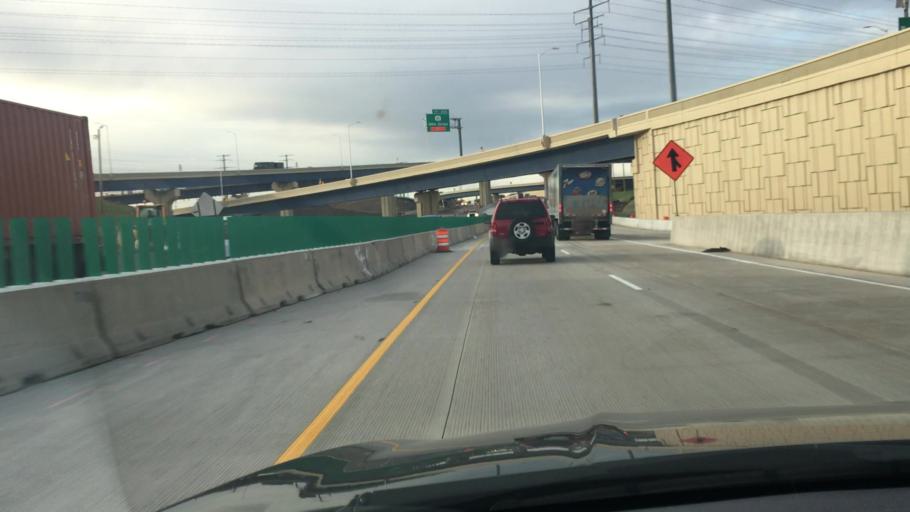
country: US
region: Wisconsin
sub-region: Milwaukee County
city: West Allis
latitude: 43.0306
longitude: -88.0343
